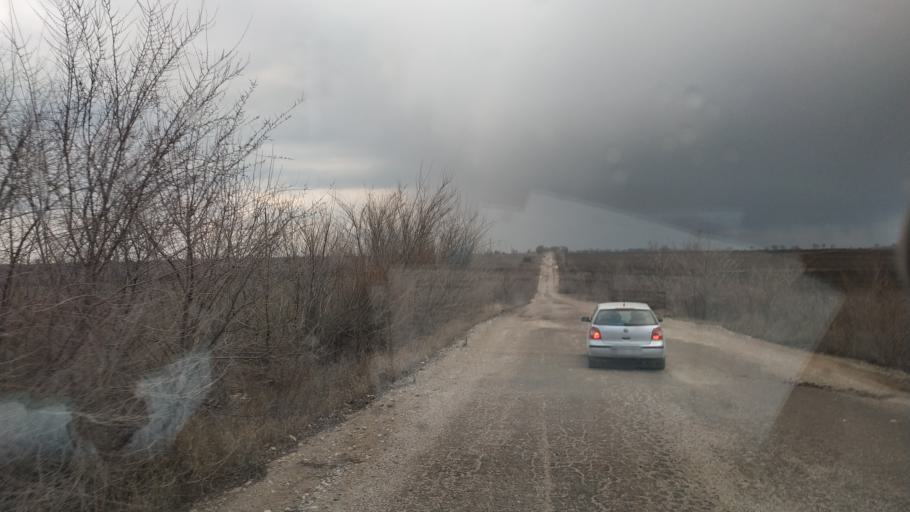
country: MD
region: Telenesti
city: Grigoriopol
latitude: 47.0595
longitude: 29.2963
